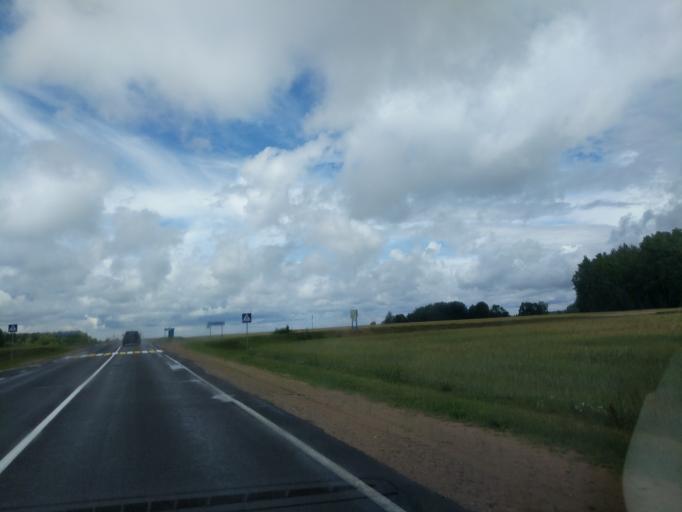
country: BY
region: Minsk
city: Il'ya
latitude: 54.3811
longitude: 27.3713
